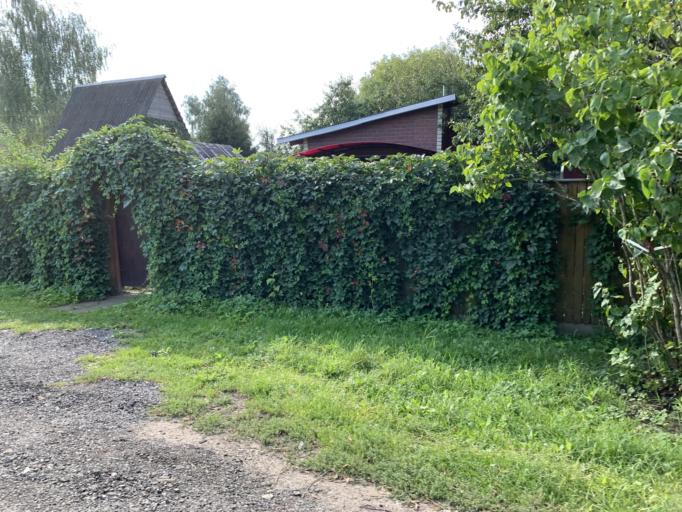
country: RU
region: Moskovskaya
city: Lesnyye Polyany
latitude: 55.9855
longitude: 37.8497
